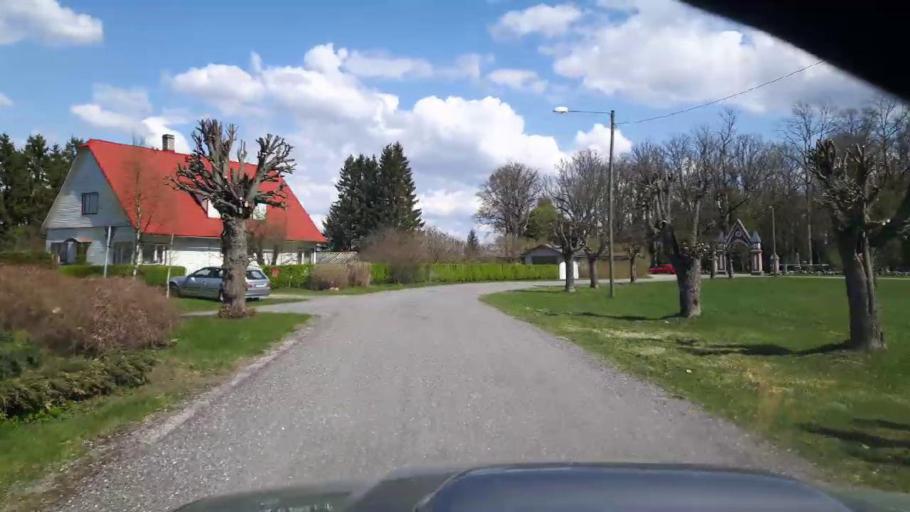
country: EE
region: Paernumaa
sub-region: Tootsi vald
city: Tootsi
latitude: 58.4829
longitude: 24.8161
